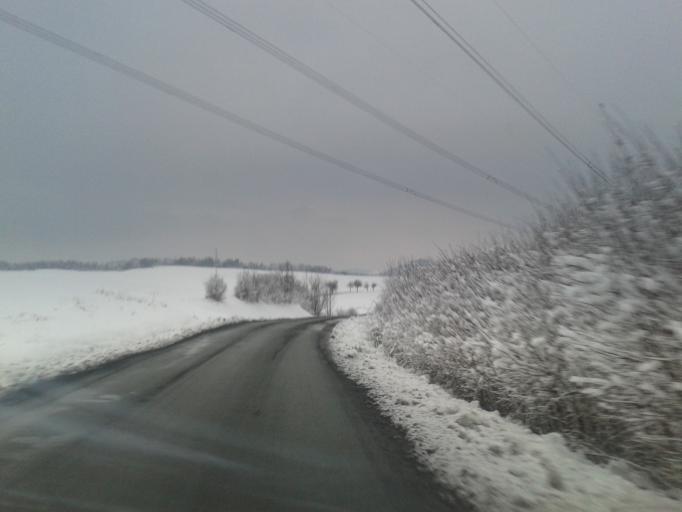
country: CZ
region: Central Bohemia
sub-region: Okres Beroun
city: Beroun
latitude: 49.9257
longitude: 14.0882
